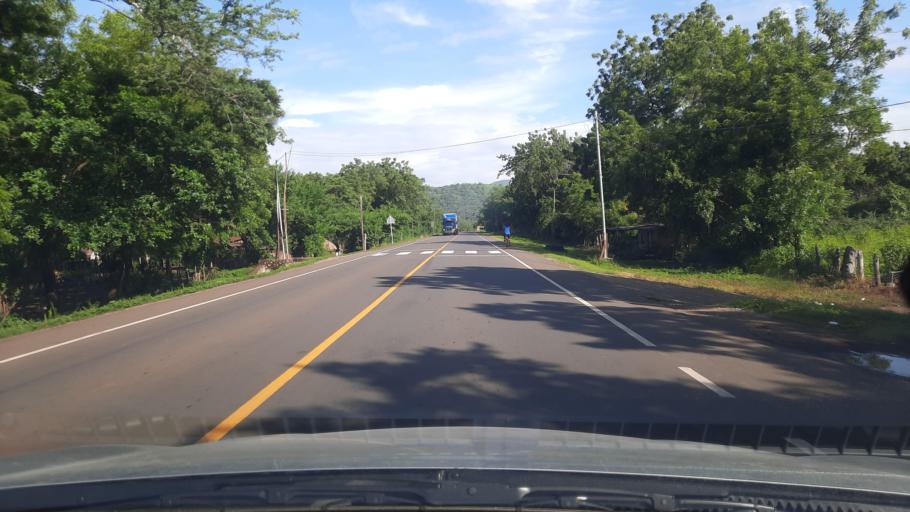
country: NI
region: Leon
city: Telica
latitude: 12.7101
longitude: -86.8730
